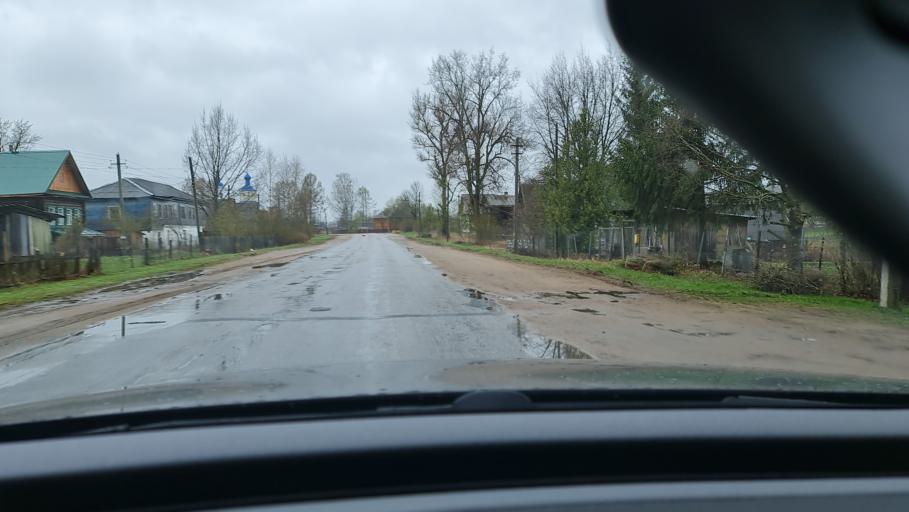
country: RU
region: Novgorod
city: Valday
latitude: 58.0362
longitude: 32.9603
